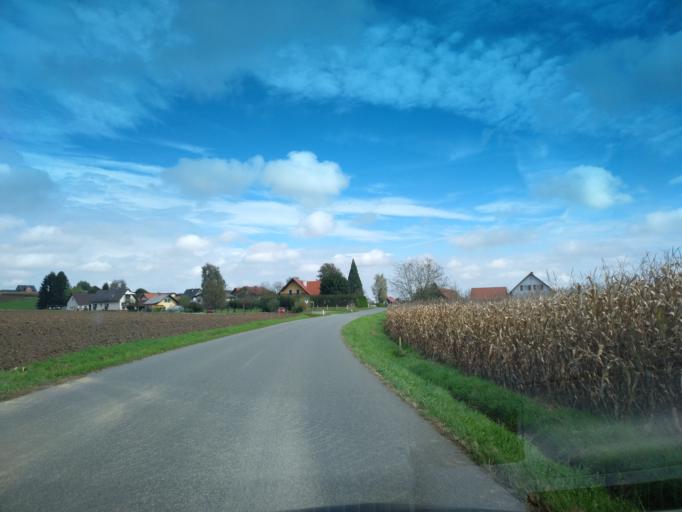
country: AT
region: Styria
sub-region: Politischer Bezirk Deutschlandsberg
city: Wettmannstatten
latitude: 46.8371
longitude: 15.3622
